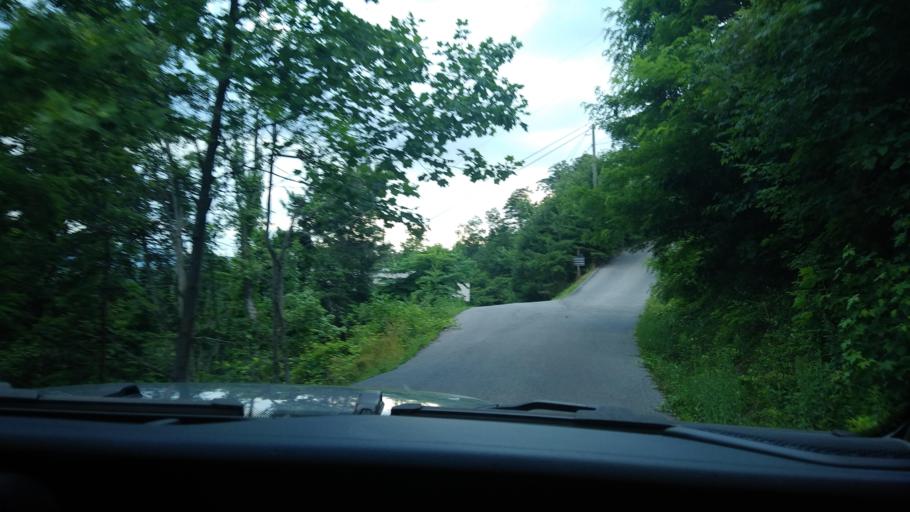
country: US
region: Tennessee
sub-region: Sevier County
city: Gatlinburg
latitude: 35.7409
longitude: -83.4826
